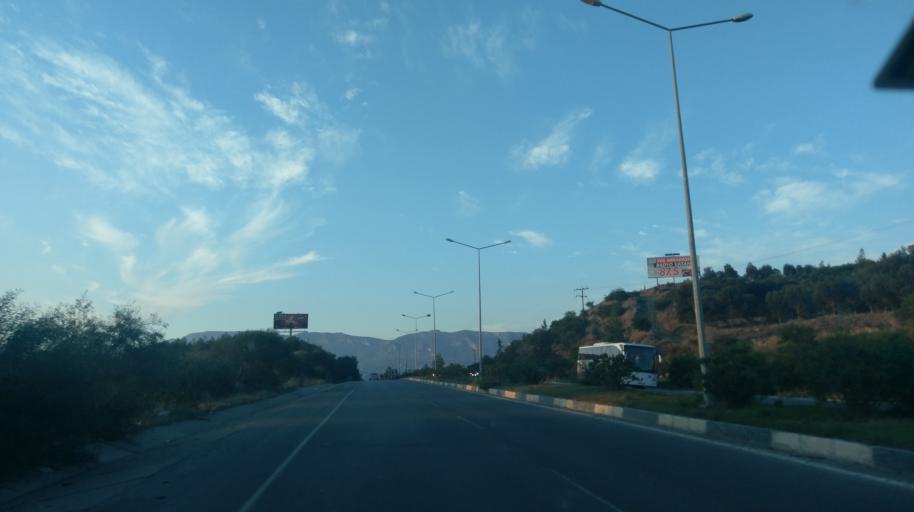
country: CY
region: Lefkosia
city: Nicosia
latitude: 35.2421
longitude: 33.3100
